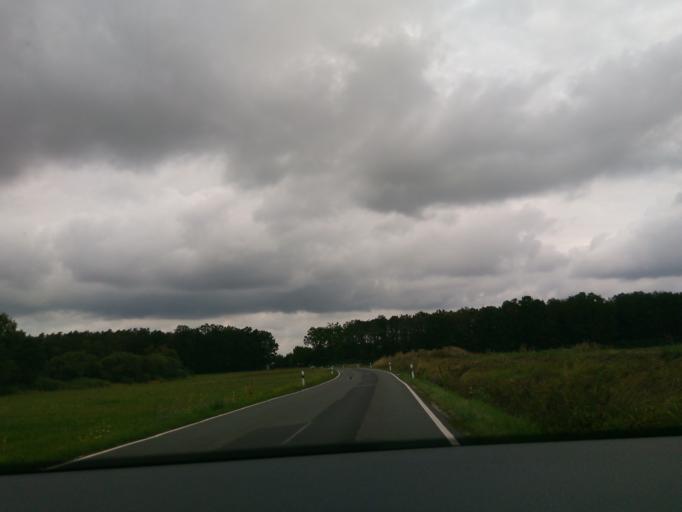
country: DE
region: Bavaria
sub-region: Regierungsbezirk Mittelfranken
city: Hochstadt an der Aisch
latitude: 49.6837
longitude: 10.8058
